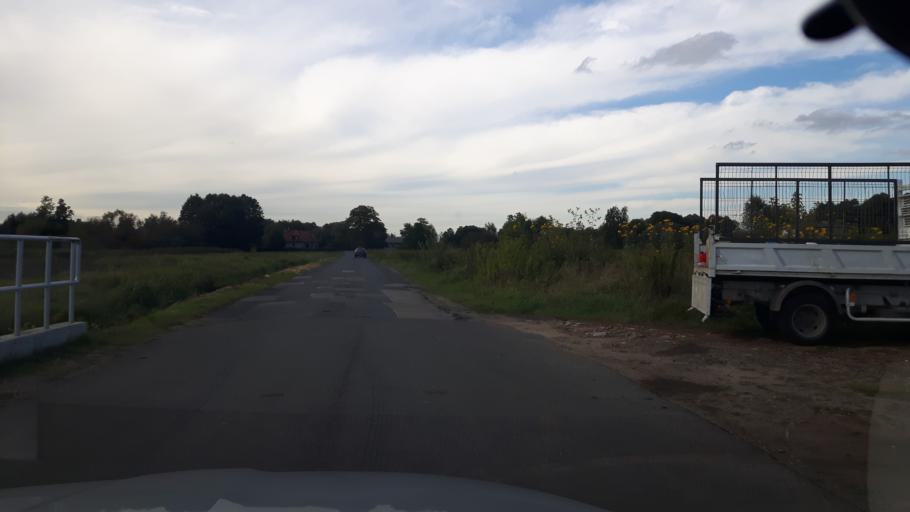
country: PL
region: Masovian Voivodeship
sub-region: Powiat legionowski
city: Stanislawow Pierwszy
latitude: 52.3507
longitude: 21.0611
